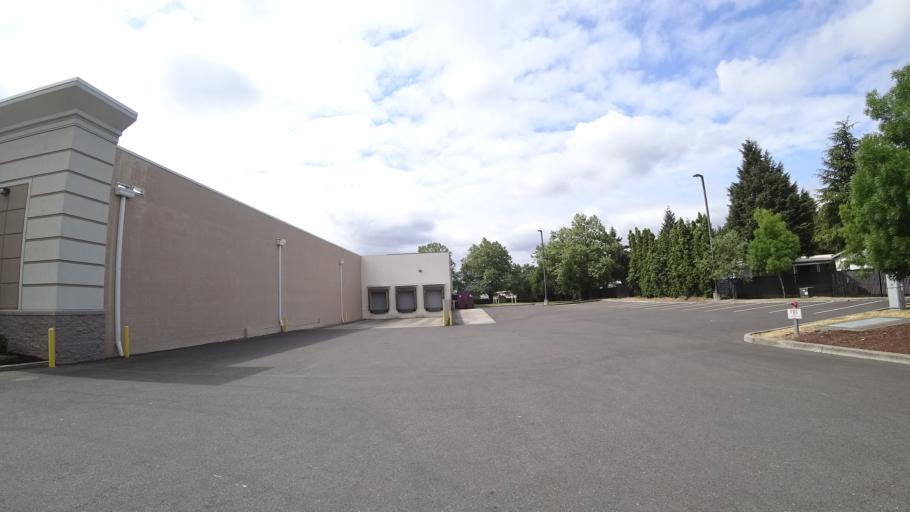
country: US
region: Washington
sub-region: Clark County
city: Vancouver
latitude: 45.6145
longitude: -122.6888
